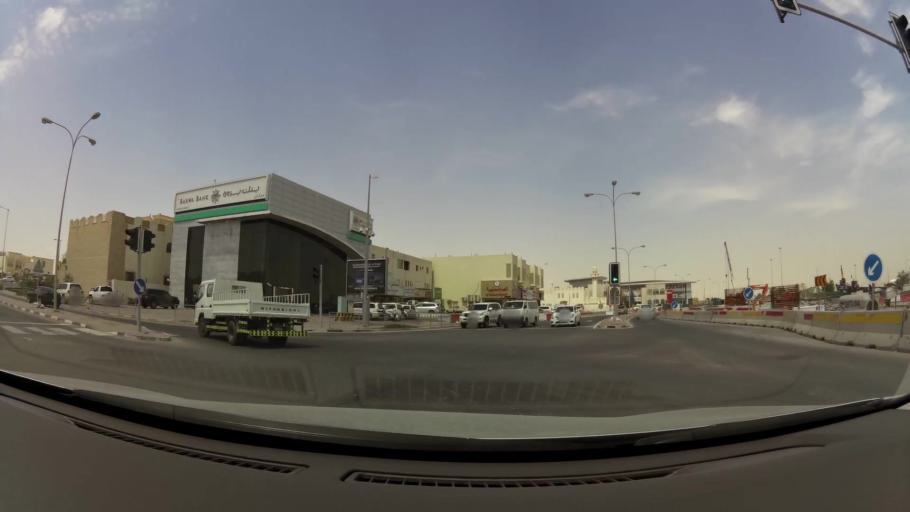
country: QA
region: Baladiyat ar Rayyan
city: Ar Rayyan
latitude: 25.2996
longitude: 51.4202
